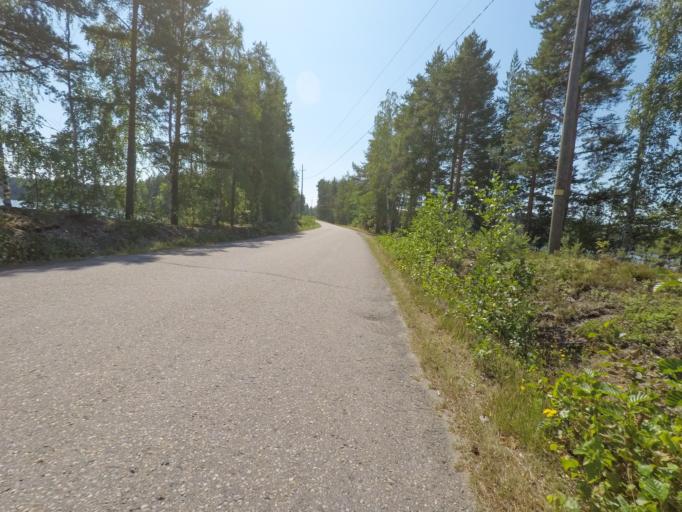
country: FI
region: Southern Savonia
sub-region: Mikkeli
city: Puumala
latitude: 61.4336
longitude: 28.1703
